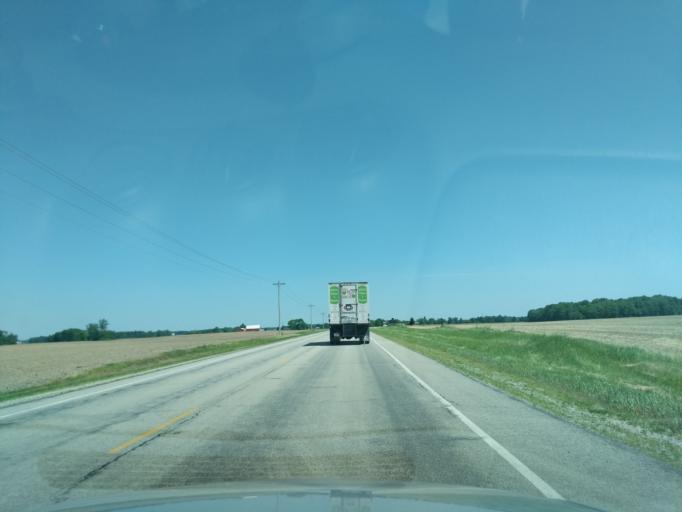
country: US
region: Indiana
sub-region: Huntington County
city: Roanoke
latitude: 41.0338
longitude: -85.4707
